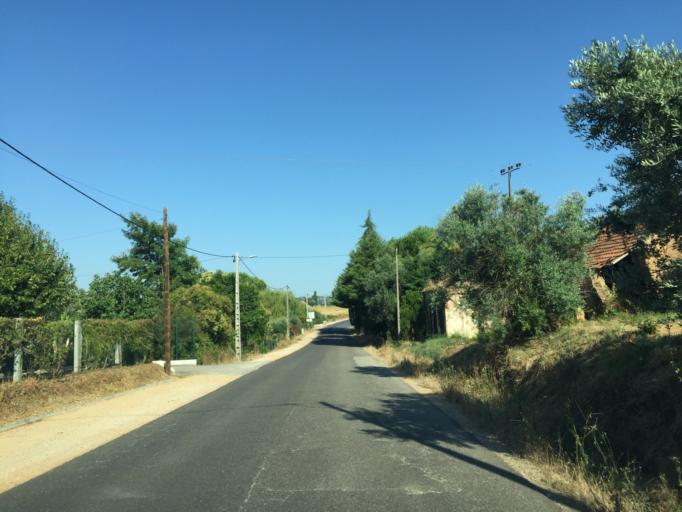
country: PT
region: Santarem
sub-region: Tomar
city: Tomar
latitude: 39.5976
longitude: -8.3802
